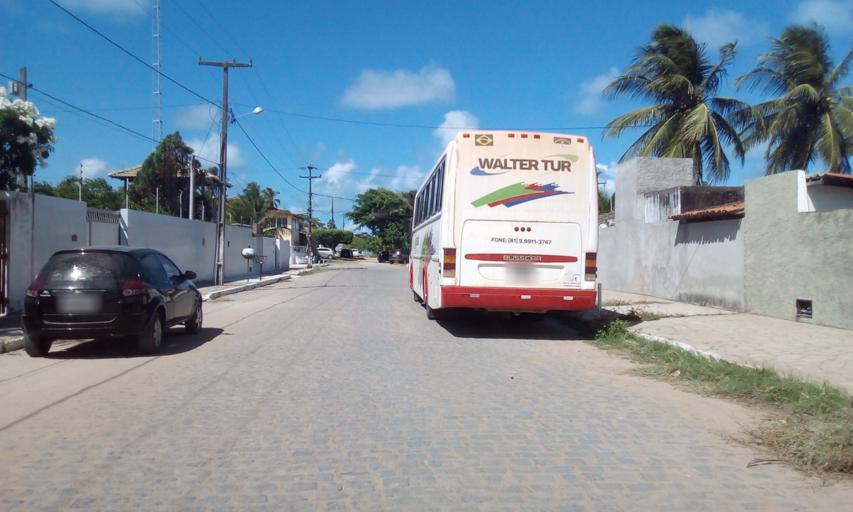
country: BR
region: Paraiba
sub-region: Conde
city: Conde
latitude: -7.2841
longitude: -34.8010
